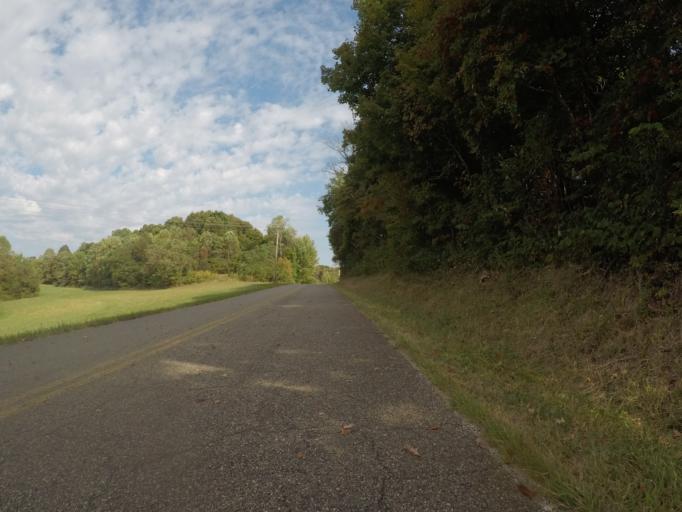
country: US
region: West Virginia
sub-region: Cabell County
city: Lesage
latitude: 38.5739
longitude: -82.4294
